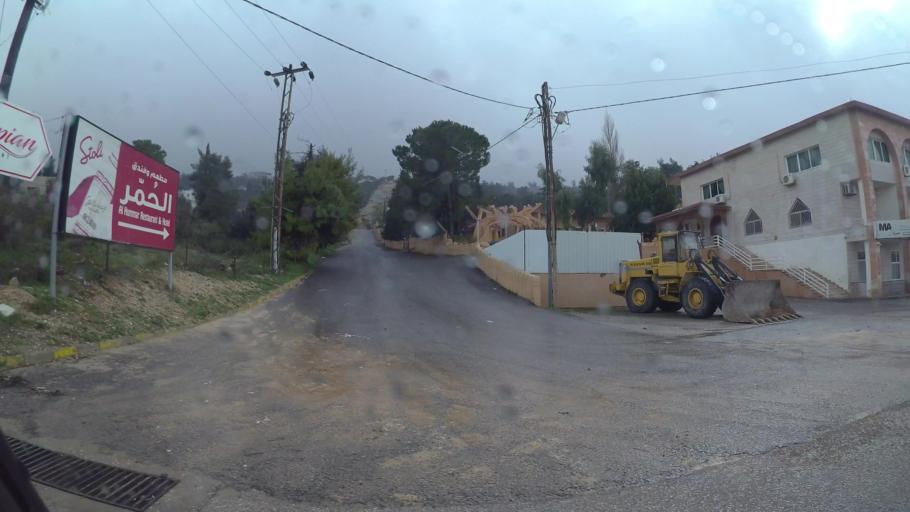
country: JO
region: Amman
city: Wadi as Sir
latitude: 32.0127
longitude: 35.8012
